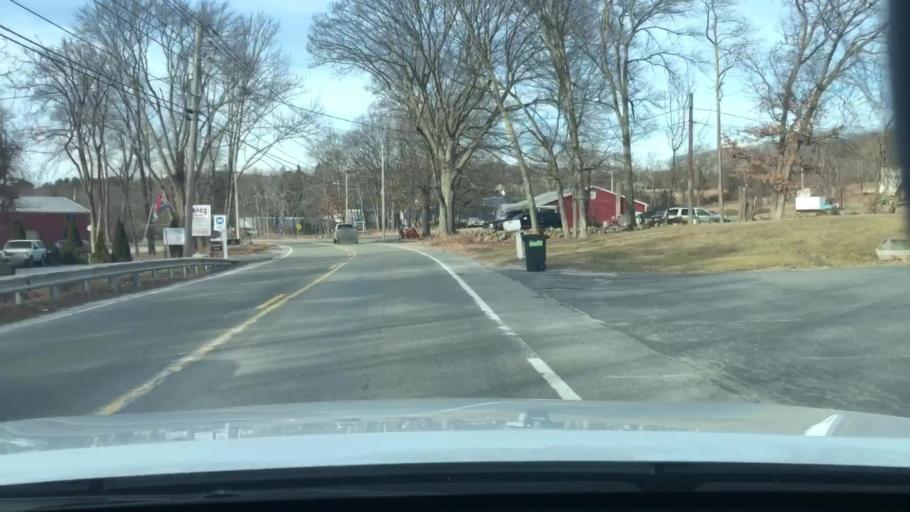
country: US
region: Massachusetts
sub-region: Worcester County
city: Upton
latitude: 42.1613
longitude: -71.5839
